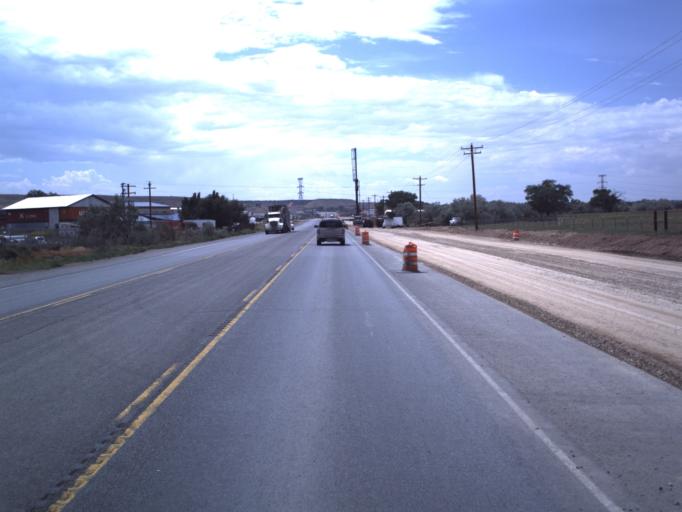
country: US
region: Utah
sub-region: Duchesne County
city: Roosevelt
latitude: 40.2678
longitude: -110.0414
